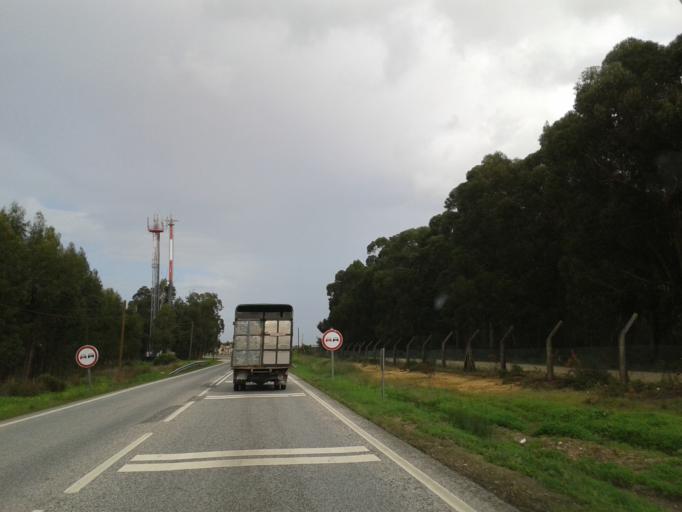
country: PT
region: Setubal
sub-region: Alcochete
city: Alcochete
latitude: 38.7806
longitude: -8.8826
